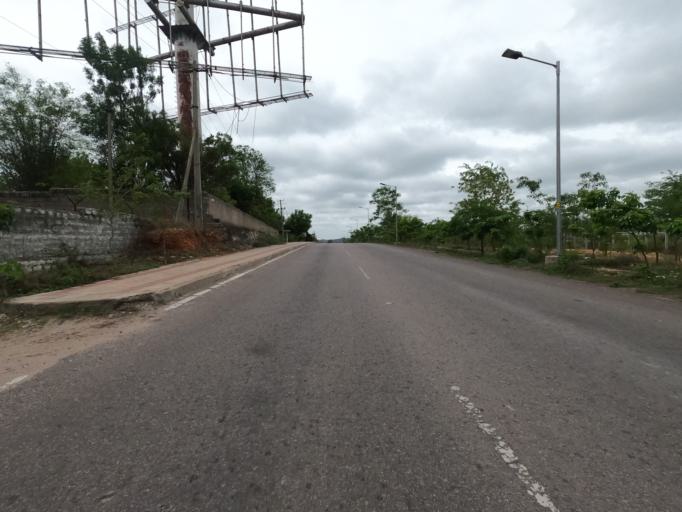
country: IN
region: Telangana
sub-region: Hyderabad
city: Hyderabad
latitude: 17.3470
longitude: 78.3621
